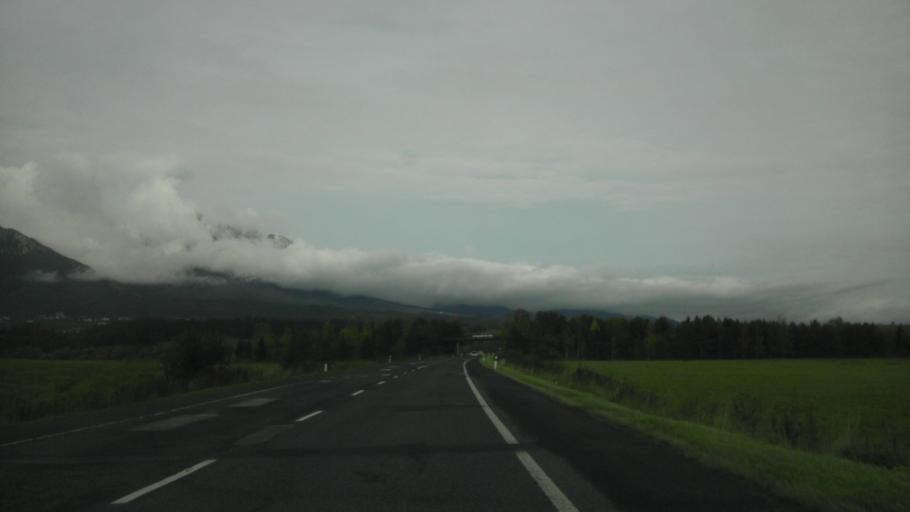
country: SK
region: Presovsky
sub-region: Okres Poprad
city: Nova Lesna
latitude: 49.0960
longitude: 20.2601
